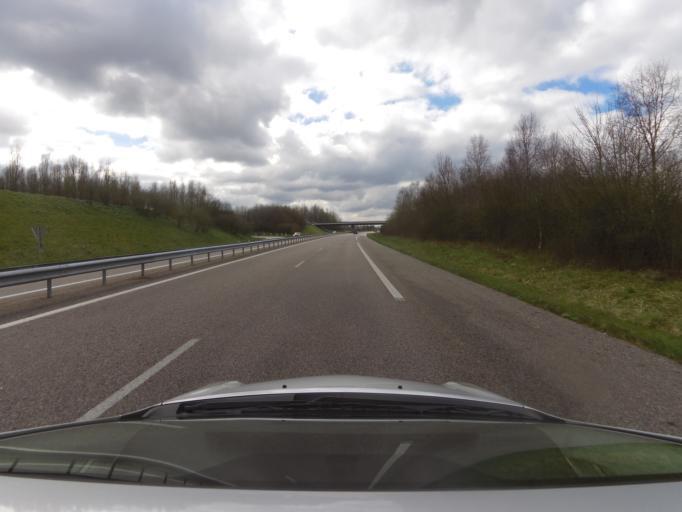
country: FR
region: Haute-Normandie
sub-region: Departement de la Seine-Maritime
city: Beuzeville-la-Grenier
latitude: 49.5831
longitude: 0.4407
